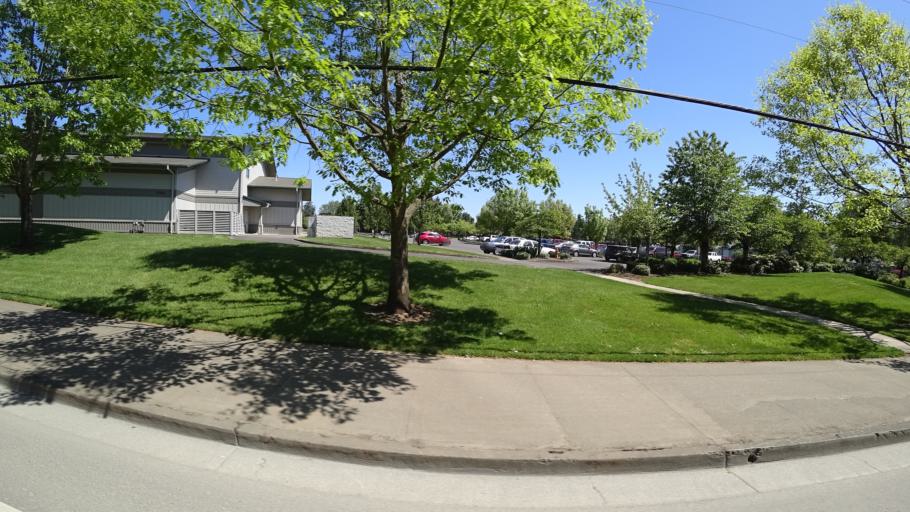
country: US
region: Oregon
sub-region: Washington County
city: Hillsboro
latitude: 45.5032
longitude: -122.9636
